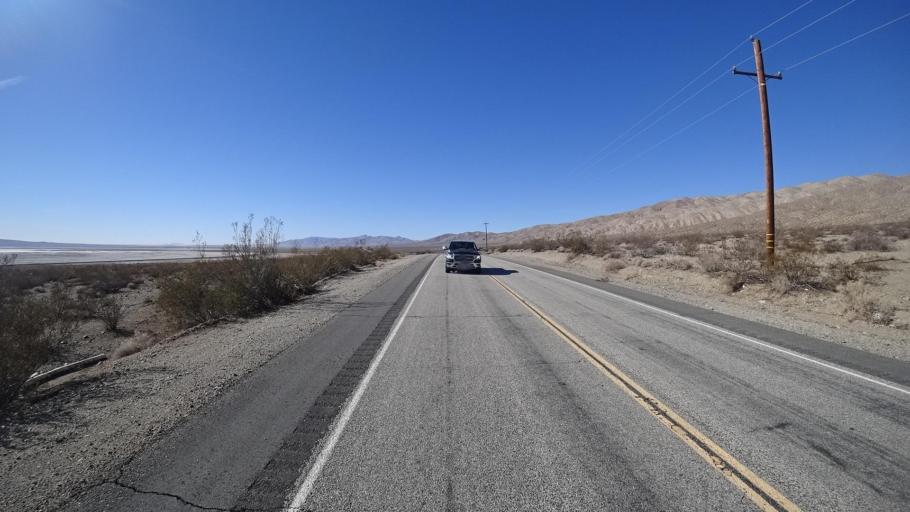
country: US
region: California
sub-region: Kern County
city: Inyokern
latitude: 35.3774
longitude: -117.8655
